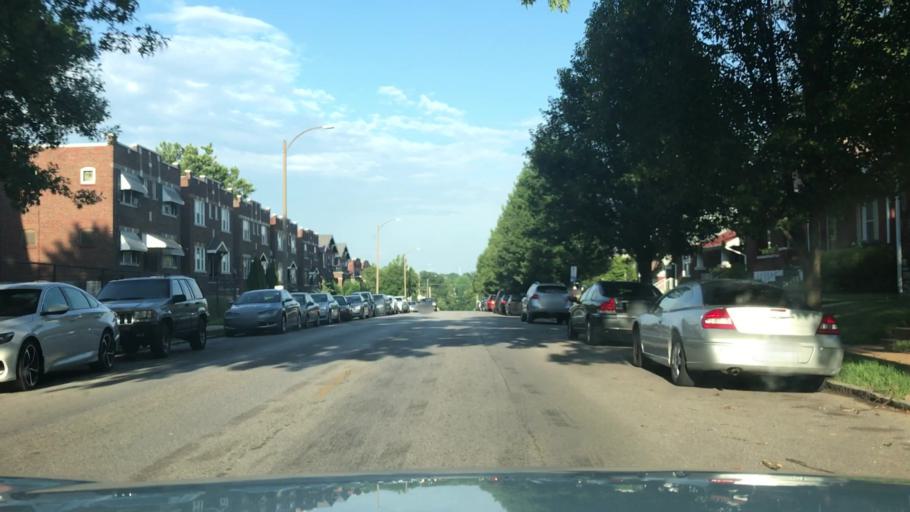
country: US
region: Missouri
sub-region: Saint Louis County
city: Lemay
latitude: 38.5812
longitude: -90.2816
